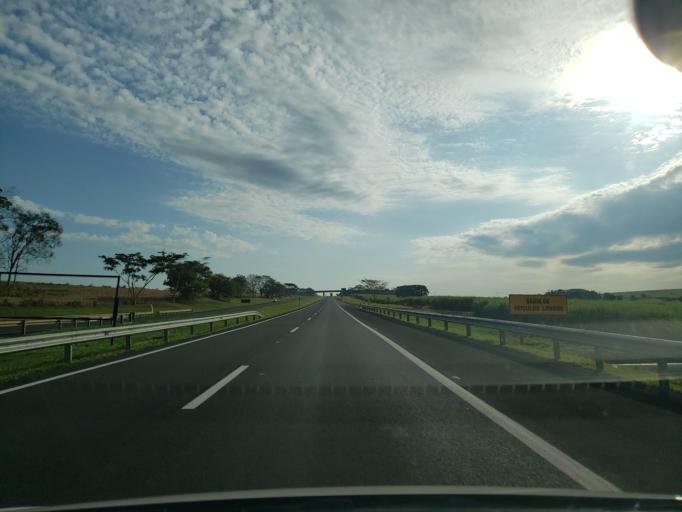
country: BR
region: Sao Paulo
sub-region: Valparaiso
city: Valparaiso
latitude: -21.2054
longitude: -50.7865
